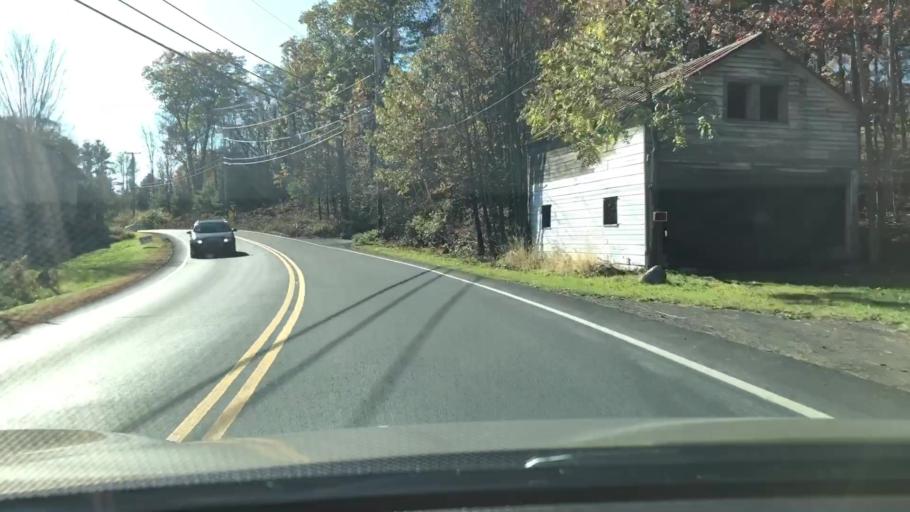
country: US
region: New York
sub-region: Ulster County
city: Zena
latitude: 42.0696
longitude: -74.0415
